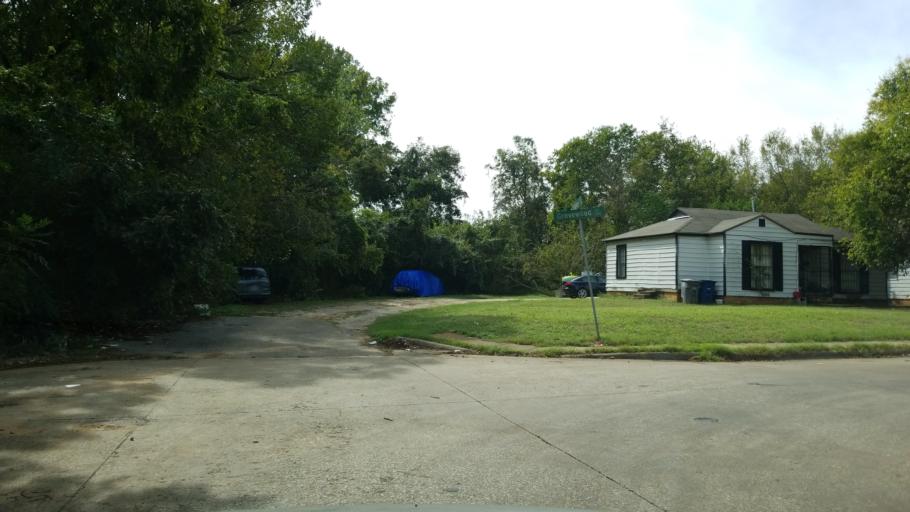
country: US
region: Texas
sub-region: Dallas County
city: Dallas
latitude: 32.7610
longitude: -96.7342
